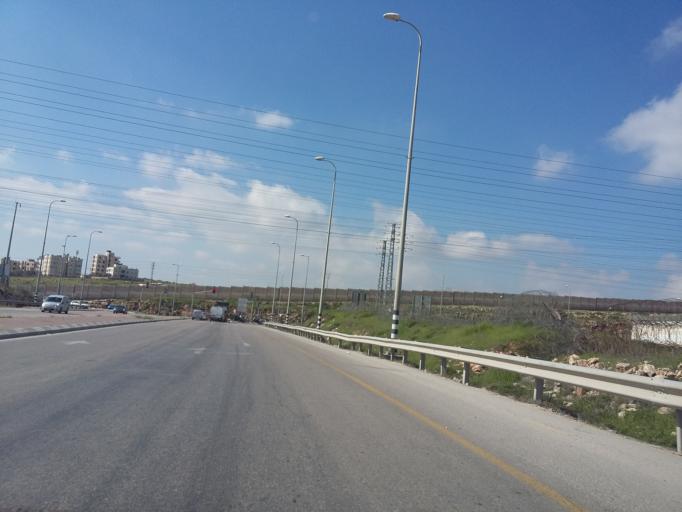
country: PS
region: West Bank
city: Qalandiya
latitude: 31.8587
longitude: 35.2097
